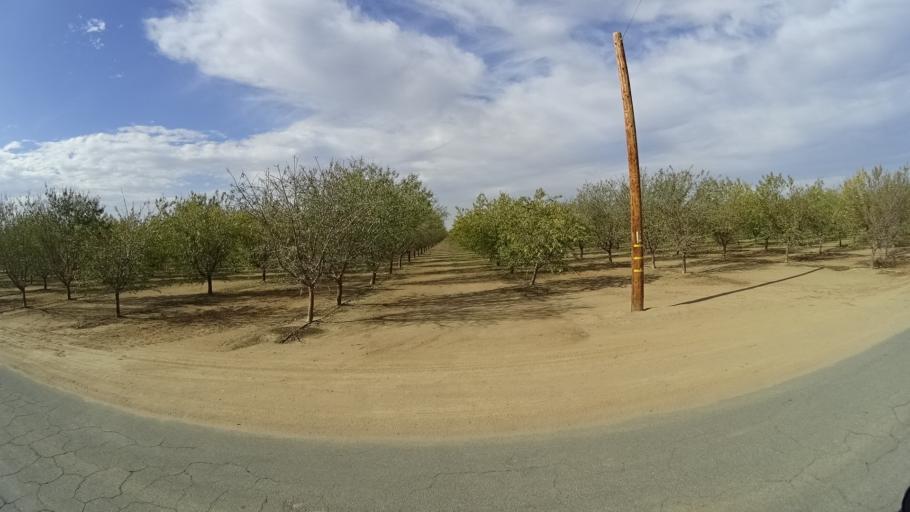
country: US
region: California
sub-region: Kern County
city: Oildale
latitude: 35.4277
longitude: -119.0745
